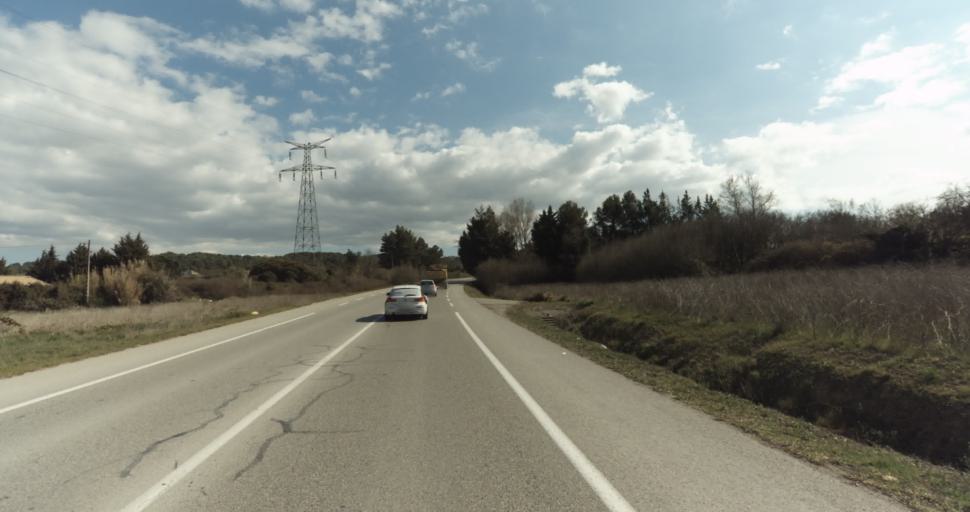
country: FR
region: Provence-Alpes-Cote d'Azur
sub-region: Departement des Bouches-du-Rhone
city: Gardanne
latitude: 43.4629
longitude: 5.4872
